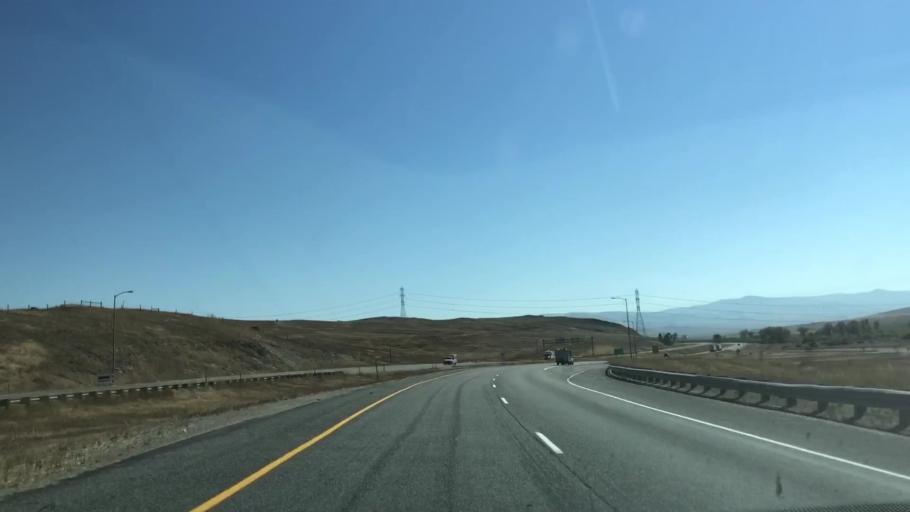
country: US
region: Montana
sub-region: Powell County
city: Deer Lodge
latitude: 46.5099
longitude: -112.7867
